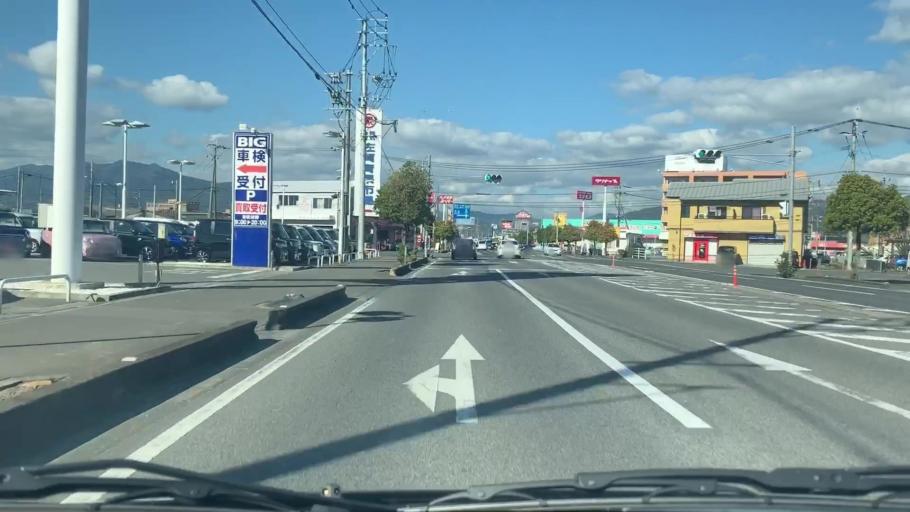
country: JP
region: Saga Prefecture
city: Saga-shi
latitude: 33.2902
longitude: 130.2870
